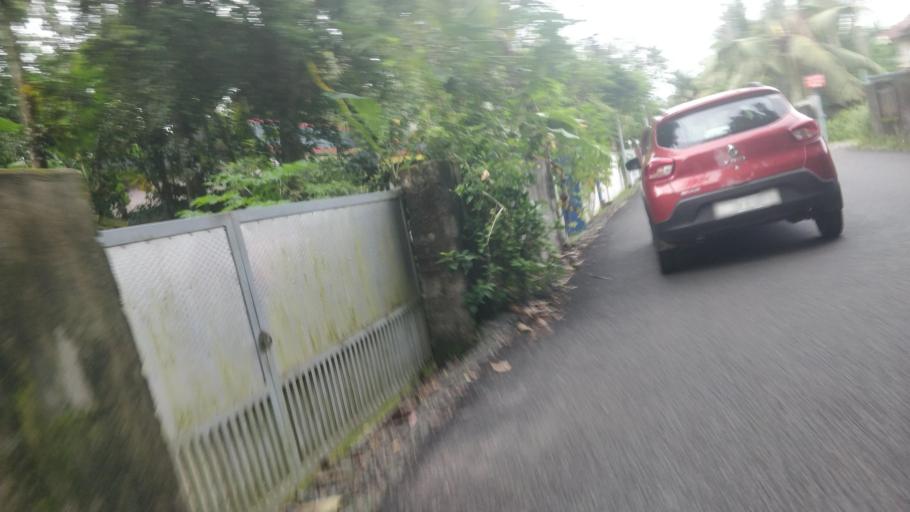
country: IN
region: Kerala
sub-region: Alappuzha
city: Shertallai
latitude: 9.6819
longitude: 76.3523
